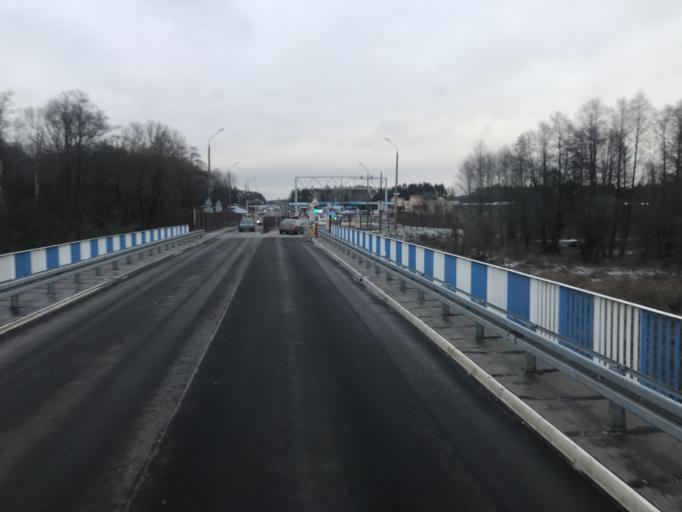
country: BY
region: Grodnenskaya
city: Vyalikaya Byerastavitsa
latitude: 53.1235
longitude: 23.8925
